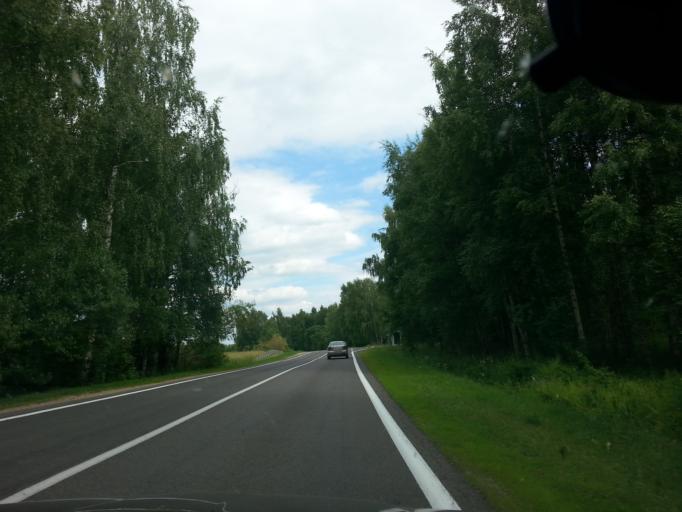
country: BY
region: Minsk
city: Myadzyel
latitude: 54.8826
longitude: 26.8472
